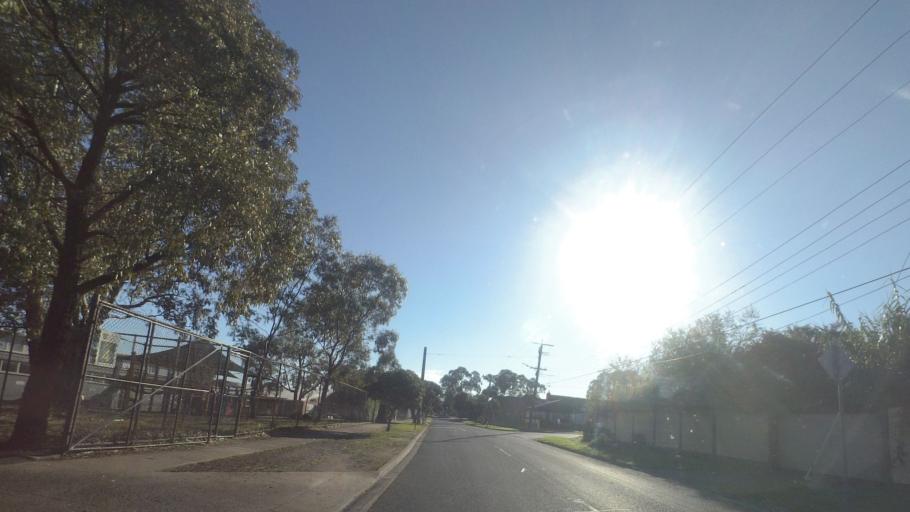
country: AU
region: Victoria
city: Macleod
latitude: -37.7251
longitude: 145.0726
